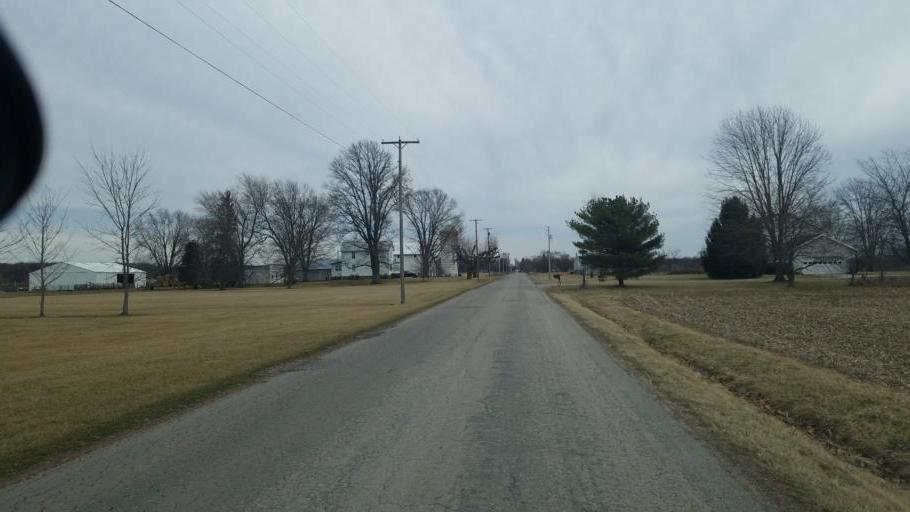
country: US
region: Ohio
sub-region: Delaware County
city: Ashley
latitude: 40.4563
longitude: -83.0161
